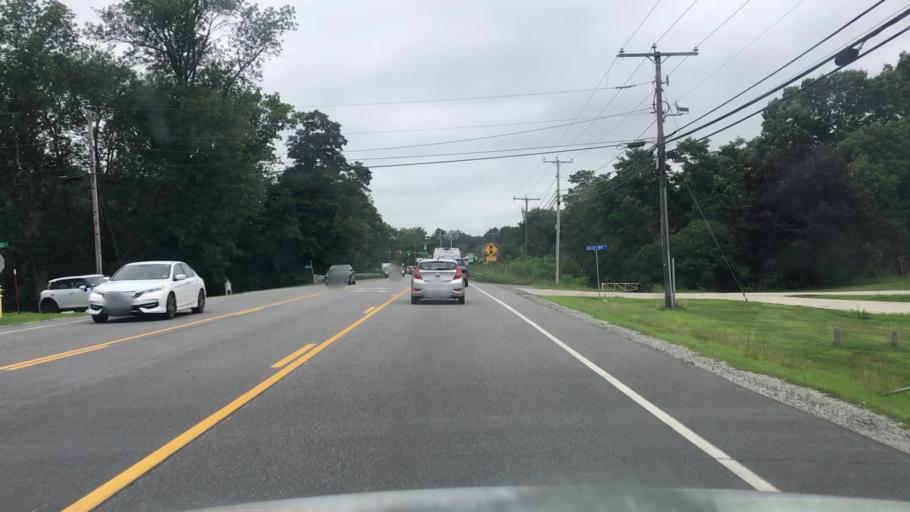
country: US
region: New Hampshire
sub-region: Rockingham County
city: Greenland
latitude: 43.0362
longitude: -70.8458
